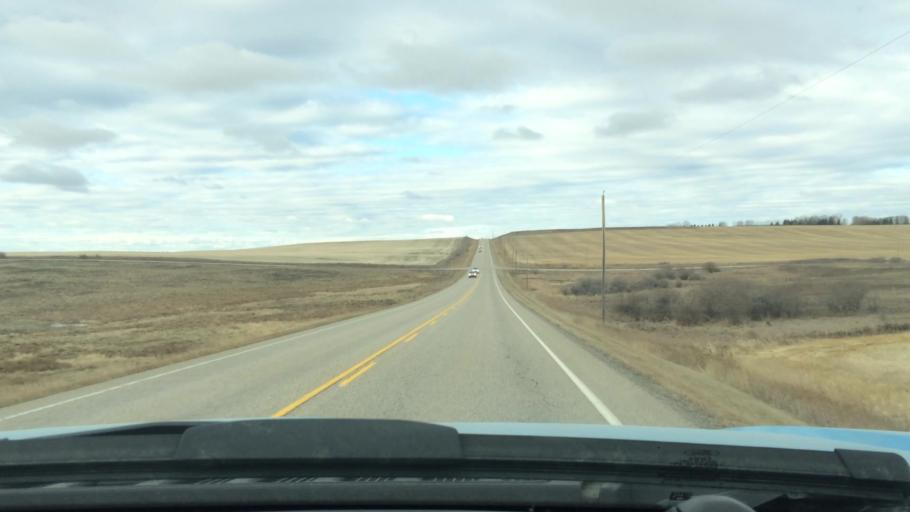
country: CA
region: Alberta
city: Airdrie
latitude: 51.2124
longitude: -114.1135
